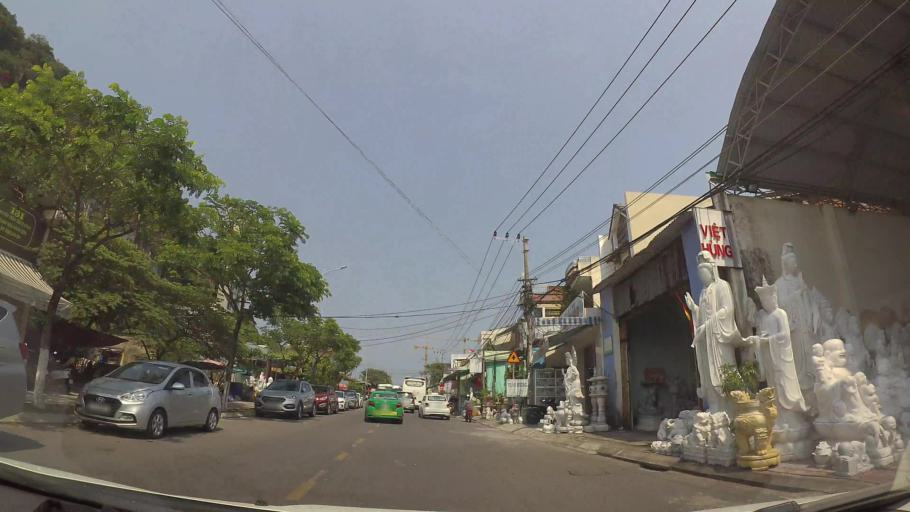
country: VN
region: Da Nang
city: Ngu Hanh Son
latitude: 16.0023
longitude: 108.2638
